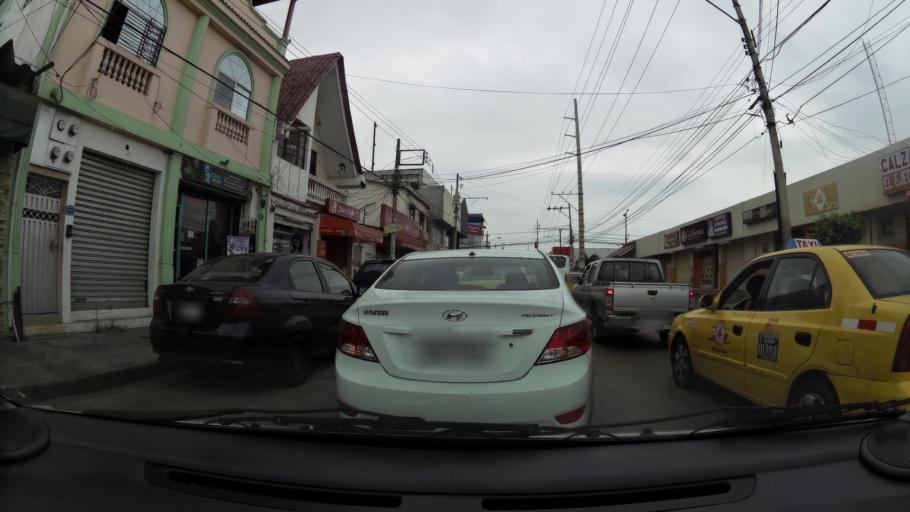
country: EC
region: Guayas
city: Eloy Alfaro
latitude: -2.1416
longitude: -79.8963
